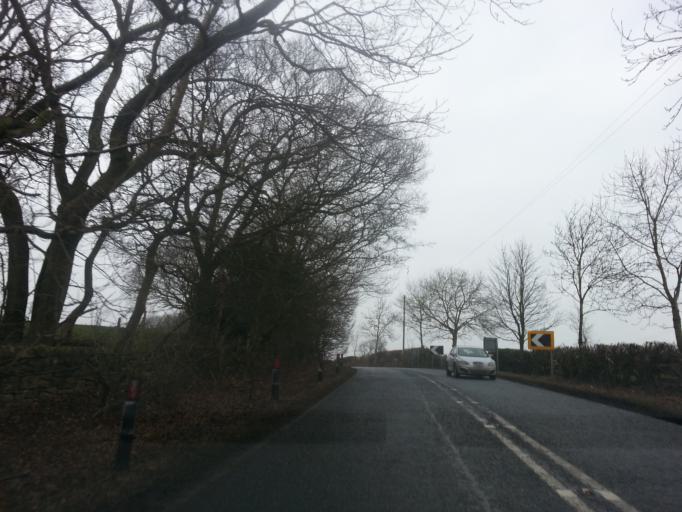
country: GB
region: England
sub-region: Darlington
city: Walworth
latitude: 54.5925
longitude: -1.6470
